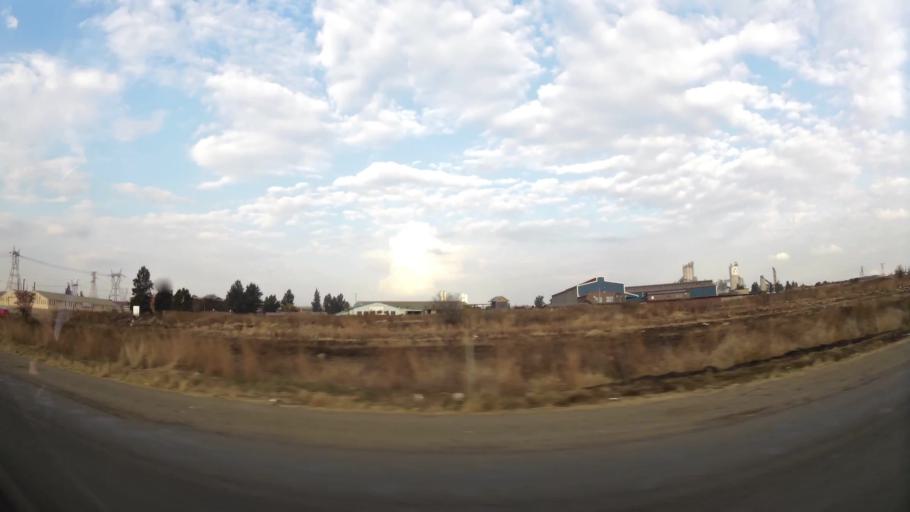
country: ZA
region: Gauteng
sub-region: Sedibeng District Municipality
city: Vanderbijlpark
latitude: -26.6671
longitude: 27.7955
